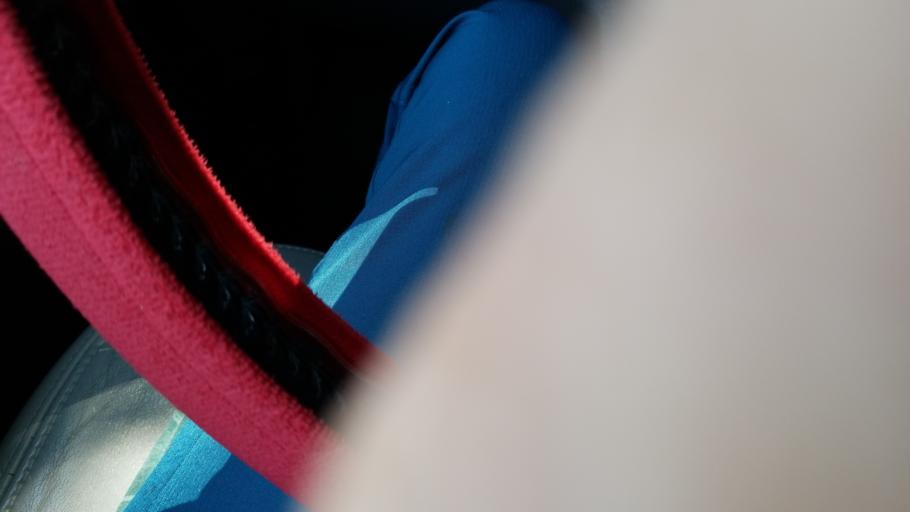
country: US
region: Texas
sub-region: Dallas County
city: Cockrell Hill
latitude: 32.7507
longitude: -96.9077
